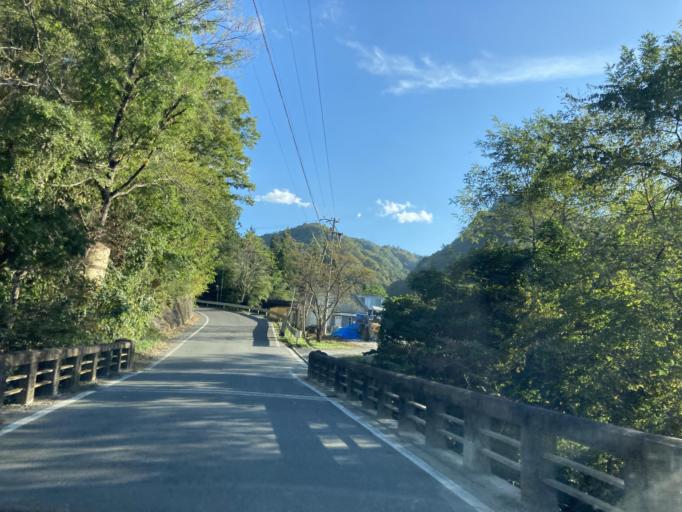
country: JP
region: Nagano
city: Omachi
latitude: 36.4431
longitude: 137.9842
